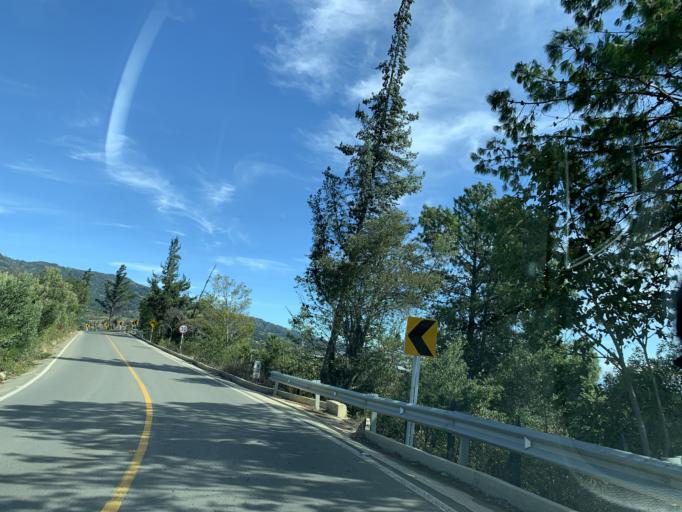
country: CO
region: Boyaca
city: Santa Sofia
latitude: 5.7043
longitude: -73.5915
